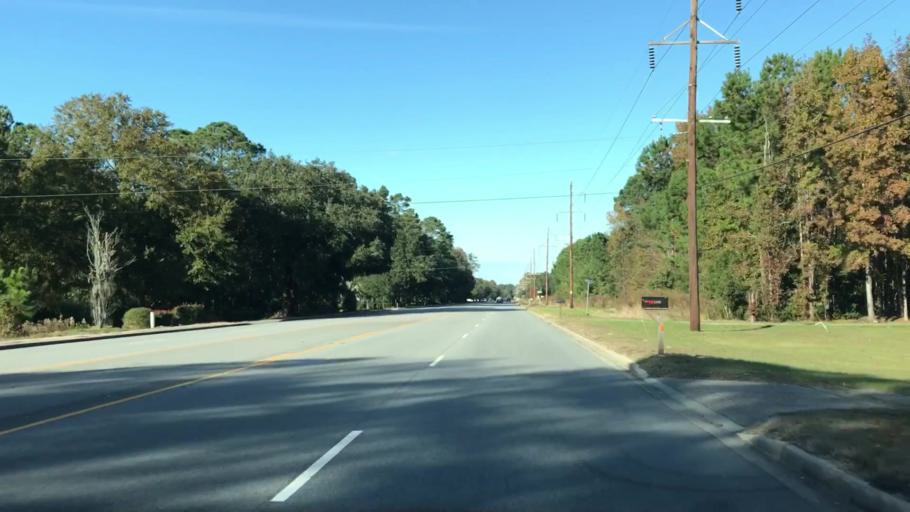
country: US
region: South Carolina
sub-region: Beaufort County
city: Laurel Bay
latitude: 32.5711
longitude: -80.7433
